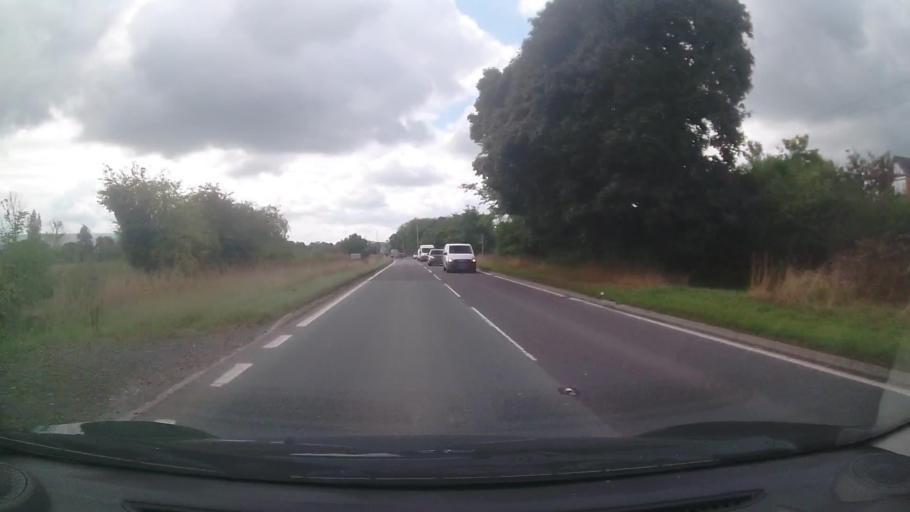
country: GB
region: England
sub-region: Shropshire
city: Pant
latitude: 52.7407
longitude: -3.0944
